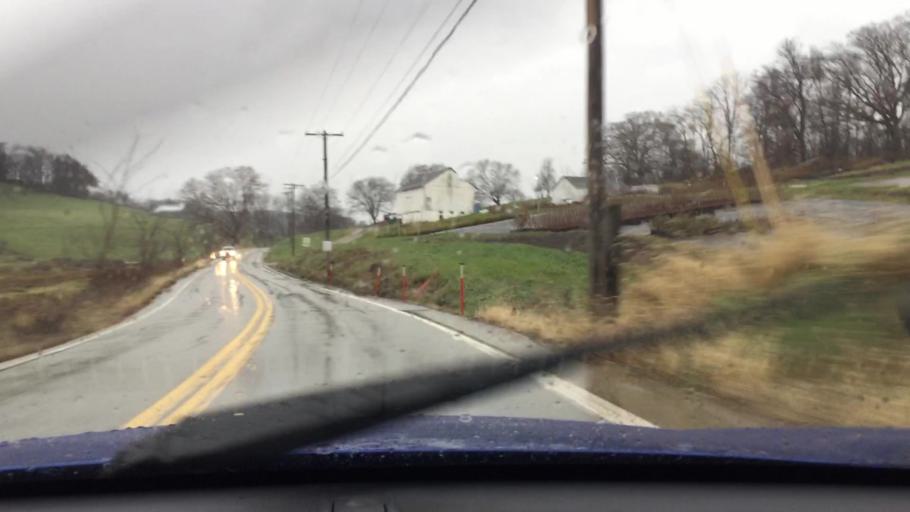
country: US
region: Pennsylvania
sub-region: Washington County
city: Ellsworth
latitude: 40.1754
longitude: -80.0932
